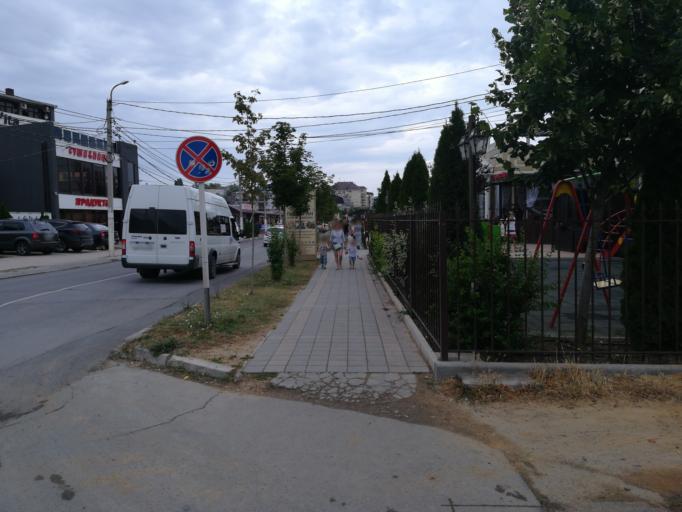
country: RU
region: Krasnodarskiy
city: Vityazevo
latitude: 44.9891
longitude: 37.2555
